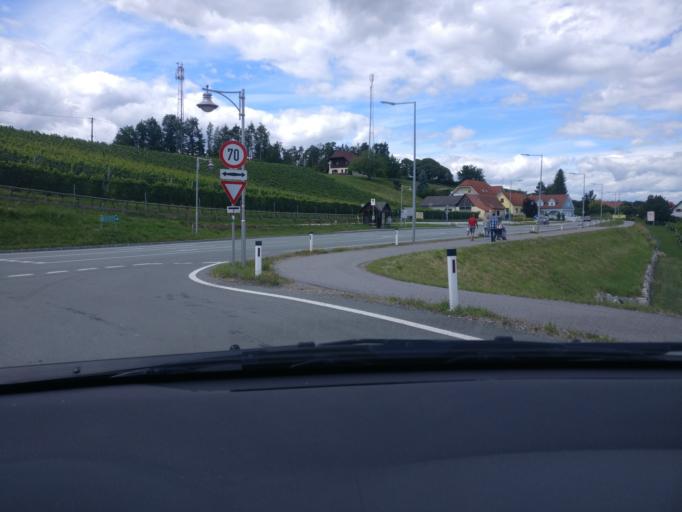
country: AT
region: Styria
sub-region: Politischer Bezirk Weiz
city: Nitscha
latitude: 47.1319
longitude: 15.7298
